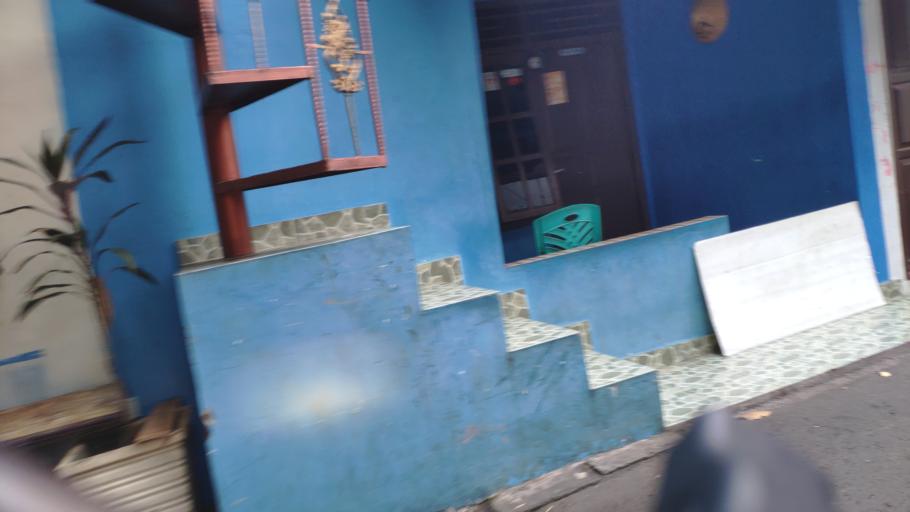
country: ID
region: Jakarta Raya
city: Jakarta
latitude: -6.2229
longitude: 106.8406
